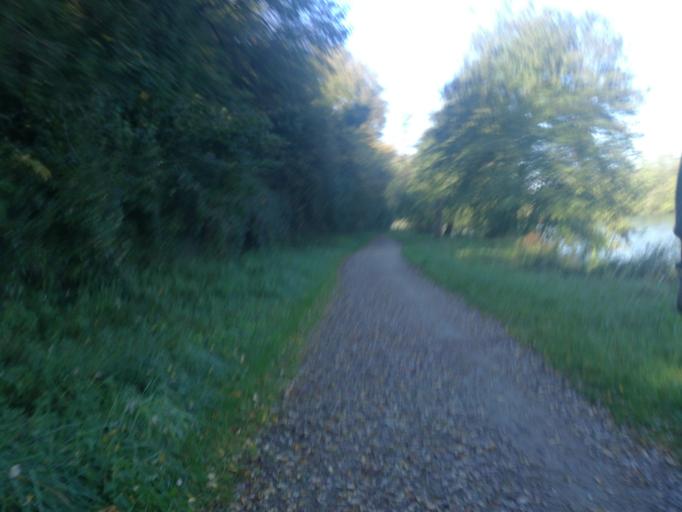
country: IT
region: Lombardy
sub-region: Provincia di Bergamo
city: Bottanuco
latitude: 45.6265
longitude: 9.5073
